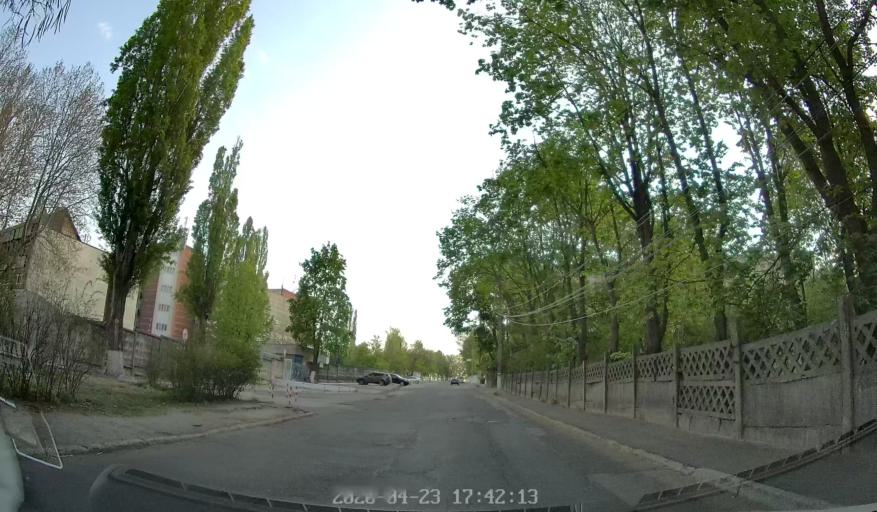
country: MD
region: Chisinau
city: Chisinau
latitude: 46.9878
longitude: 28.8340
